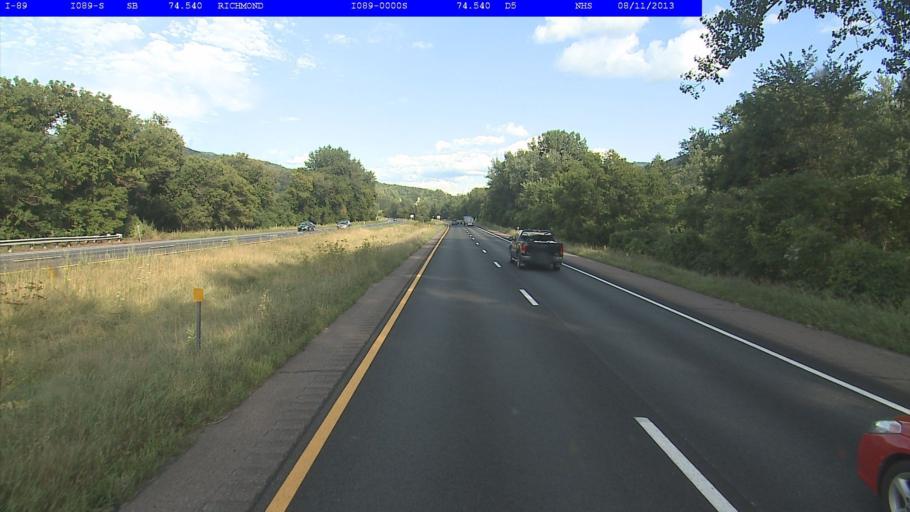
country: US
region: Vermont
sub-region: Chittenden County
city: Jericho
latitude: 44.3908
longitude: -72.9537
